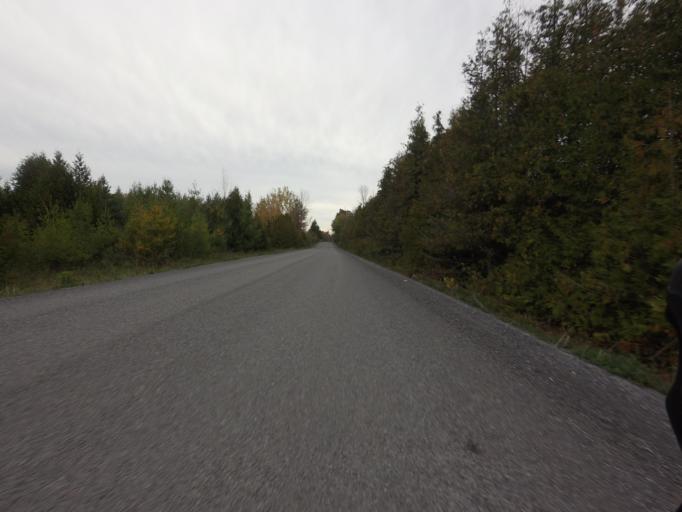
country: CA
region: Ontario
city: Bells Corners
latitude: 45.0859
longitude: -75.7568
